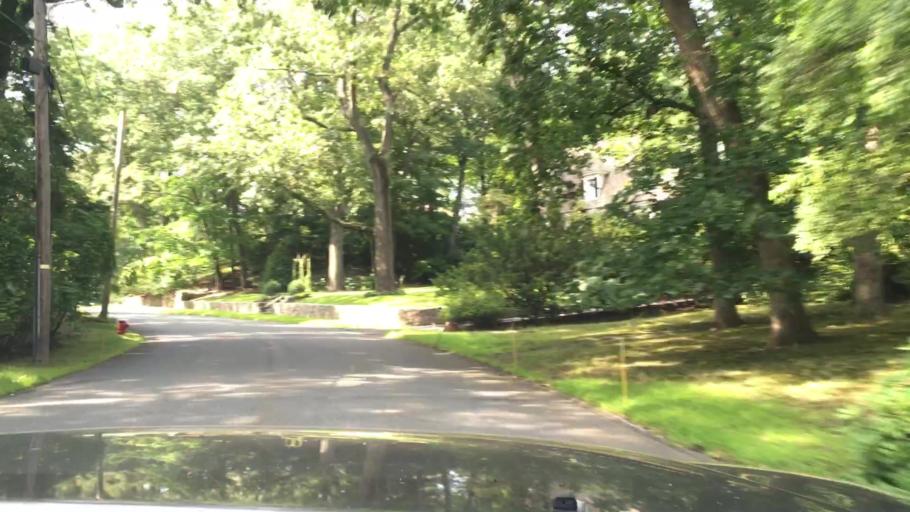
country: US
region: Massachusetts
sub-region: Norfolk County
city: Wellesley
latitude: 42.3123
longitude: -71.2799
